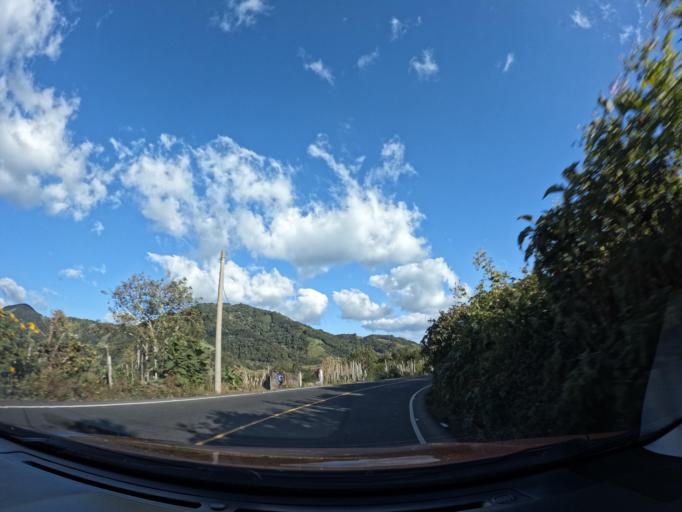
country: GT
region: Sacatepequez
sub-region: Municipio de Santa Maria de Jesus
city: Santa Maria de Jesus
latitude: 14.4805
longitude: -90.7004
